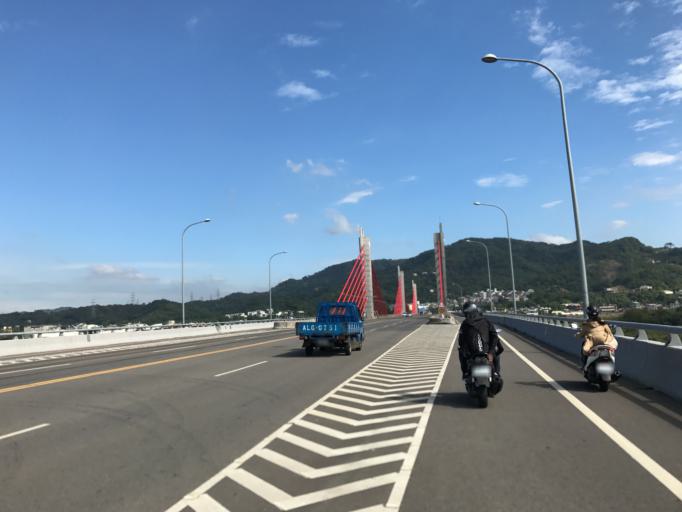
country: TW
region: Taiwan
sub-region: Hsinchu
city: Zhubei
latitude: 24.7459
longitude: 121.0911
